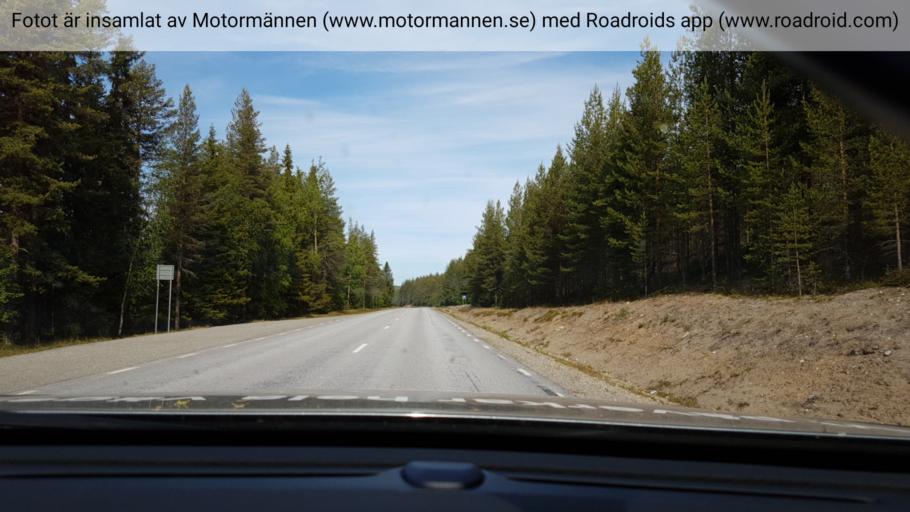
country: SE
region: Vaesterbotten
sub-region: Asele Kommun
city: Asele
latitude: 64.2020
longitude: 17.0308
